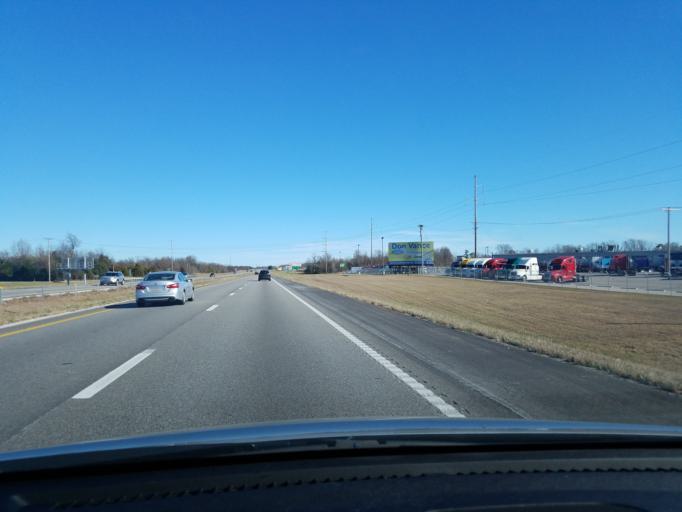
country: US
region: Missouri
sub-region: Greene County
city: Strafford
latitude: 37.2543
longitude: -93.1709
